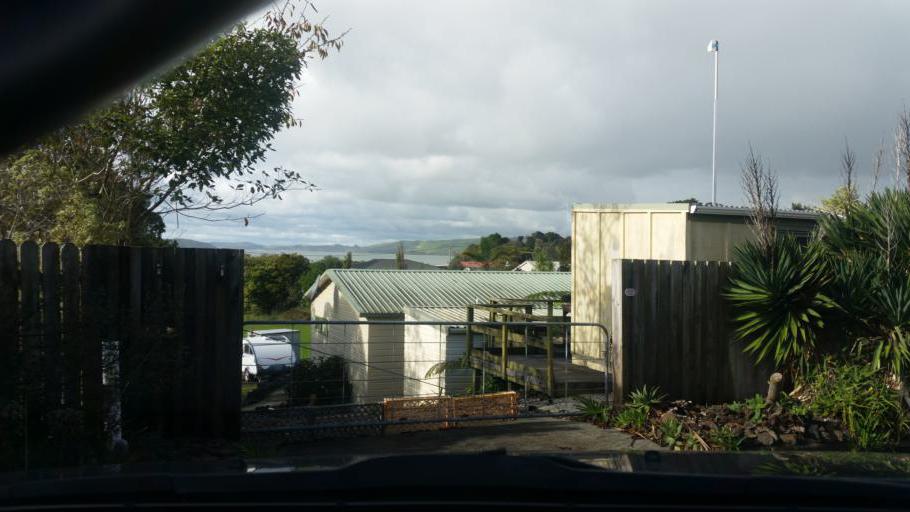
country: NZ
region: Auckland
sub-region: Auckland
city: Wellsford
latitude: -36.2545
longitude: 174.2441
